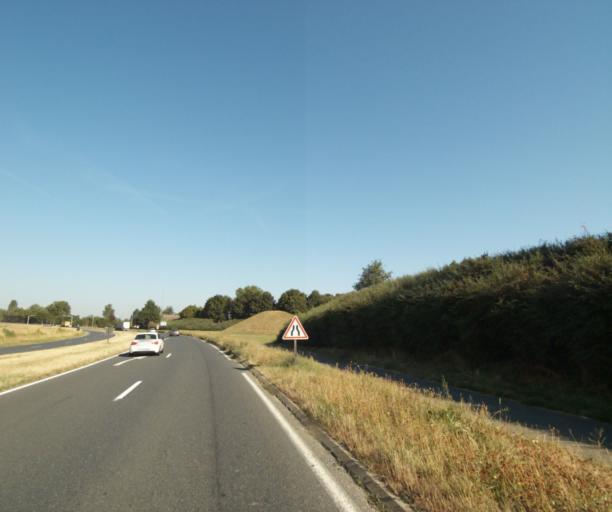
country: FR
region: Ile-de-France
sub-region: Departement de Seine-et-Marne
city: Moissy-Cramayel
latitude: 48.6250
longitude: 2.5778
